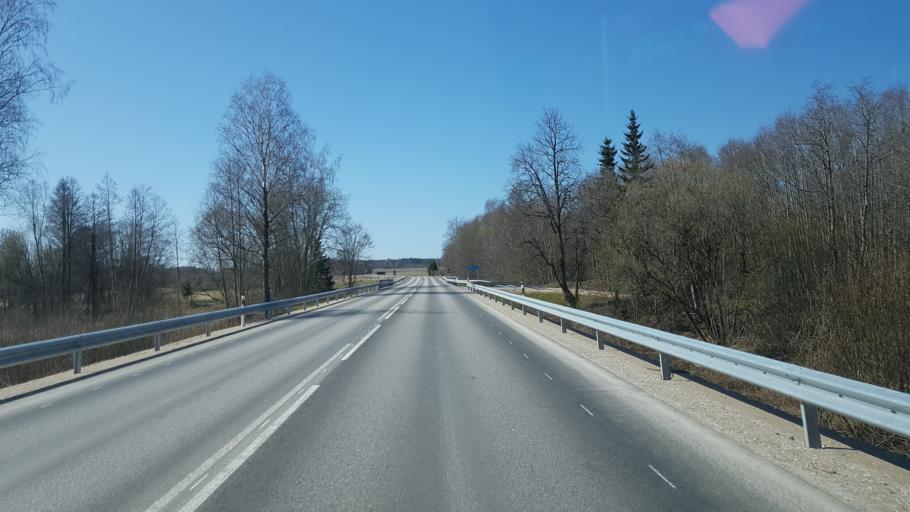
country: EE
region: Viljandimaa
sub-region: Abja vald
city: Abja-Paluoja
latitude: 58.3356
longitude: 25.3375
